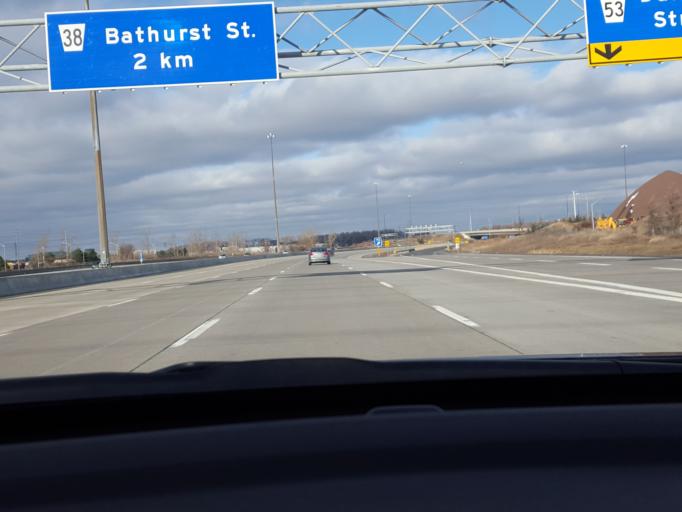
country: CA
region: Ontario
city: Concord
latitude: 43.8108
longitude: -79.4797
